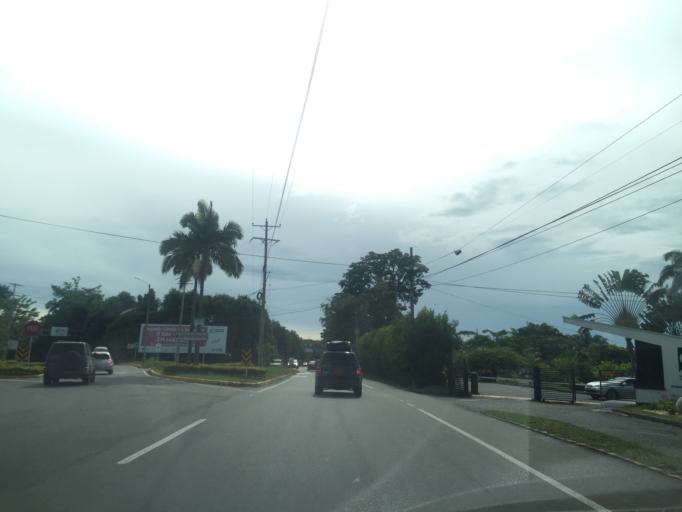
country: CO
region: Quindio
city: La Tebaida
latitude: 4.4713
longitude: -75.7643
